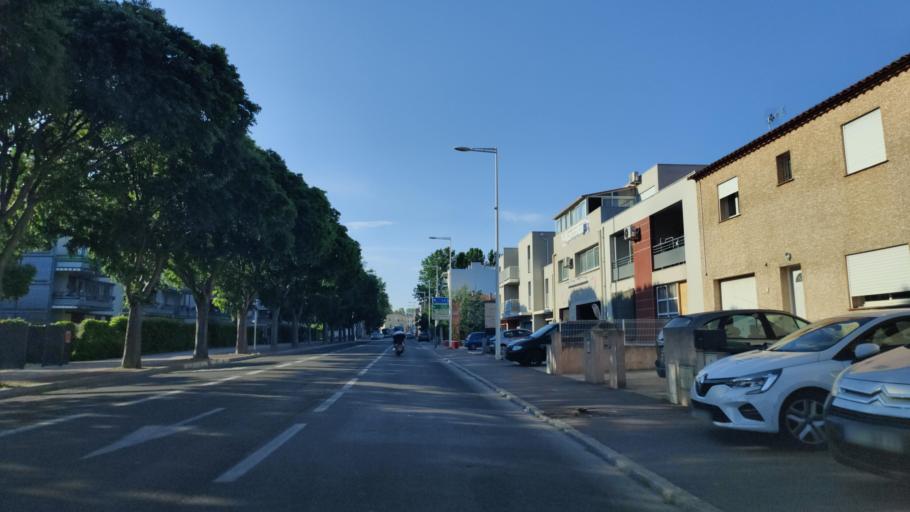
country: FR
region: Languedoc-Roussillon
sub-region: Departement des Pyrenees-Orientales
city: Perpignan
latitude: 42.7184
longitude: 2.8872
